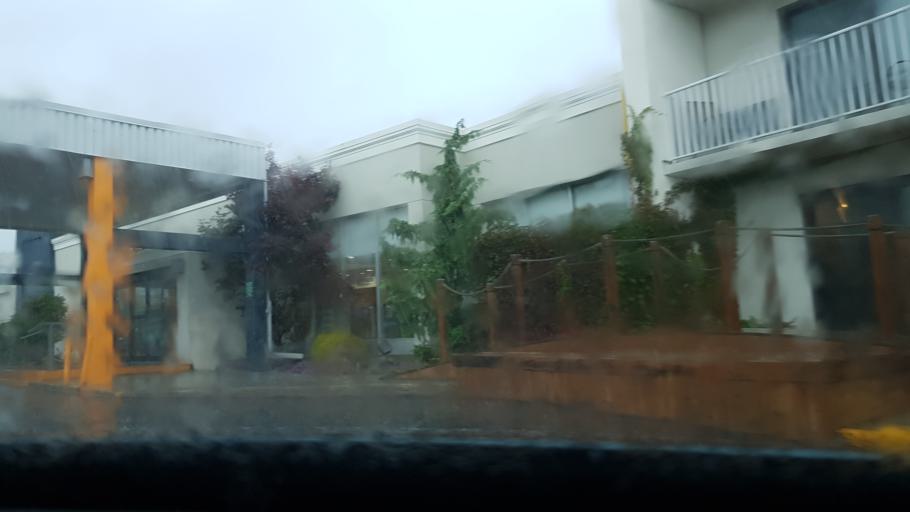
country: CA
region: Ontario
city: Peterborough
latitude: 44.2981
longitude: -78.3194
